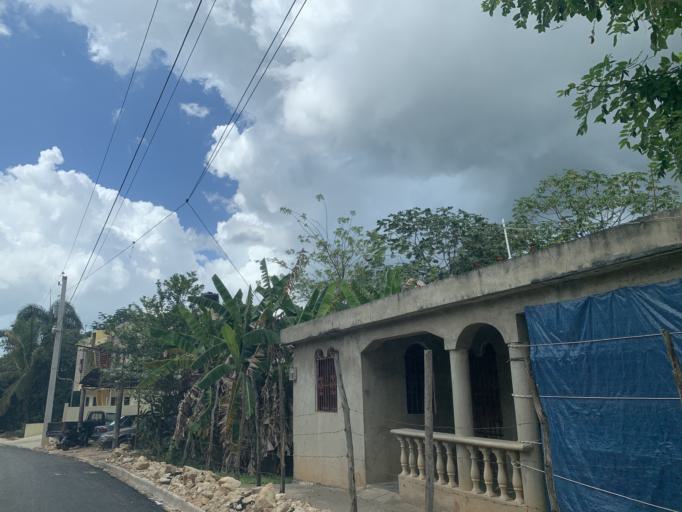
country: DO
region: Monte Plata
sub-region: Yamasa
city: Yamasa
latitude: 18.7795
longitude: -70.0252
